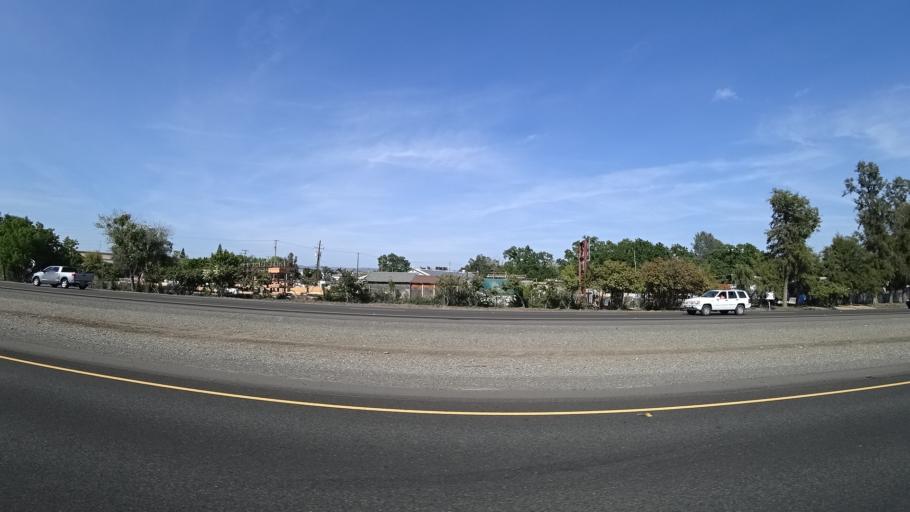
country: US
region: California
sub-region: Butte County
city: Chico
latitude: 39.7103
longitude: -121.7963
